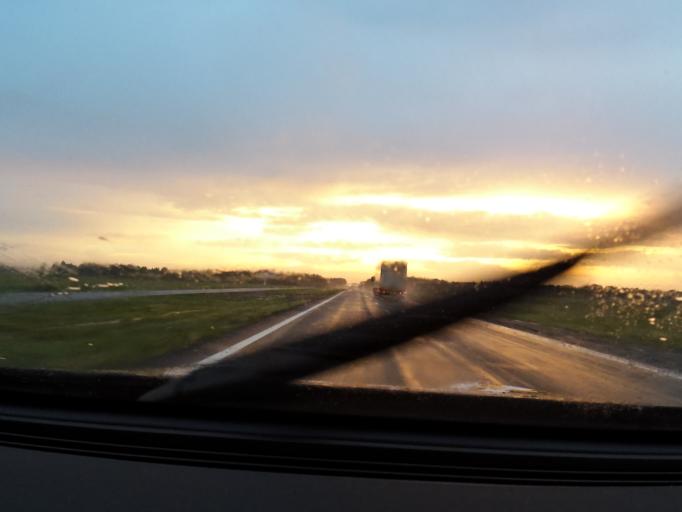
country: RU
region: Tatarstan
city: Yelabuga
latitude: 55.7908
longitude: 52.1612
